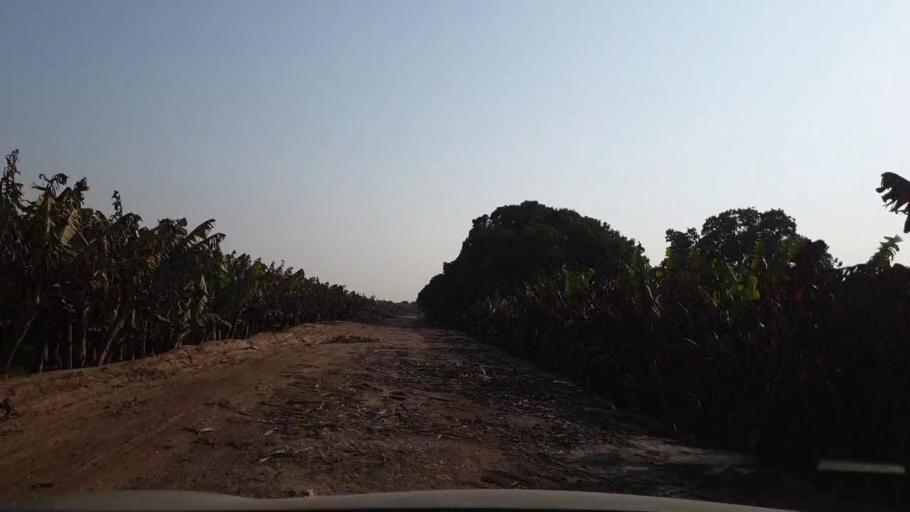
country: PK
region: Sindh
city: Tando Allahyar
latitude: 25.5722
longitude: 68.7642
